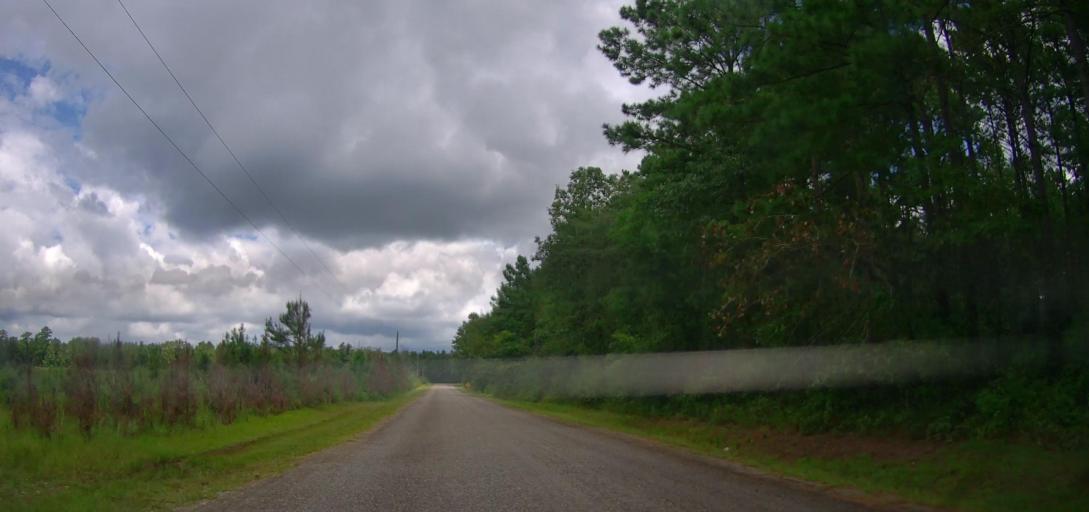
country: US
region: Georgia
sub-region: Pulaski County
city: Hawkinsville
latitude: 32.3303
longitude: -83.5262
